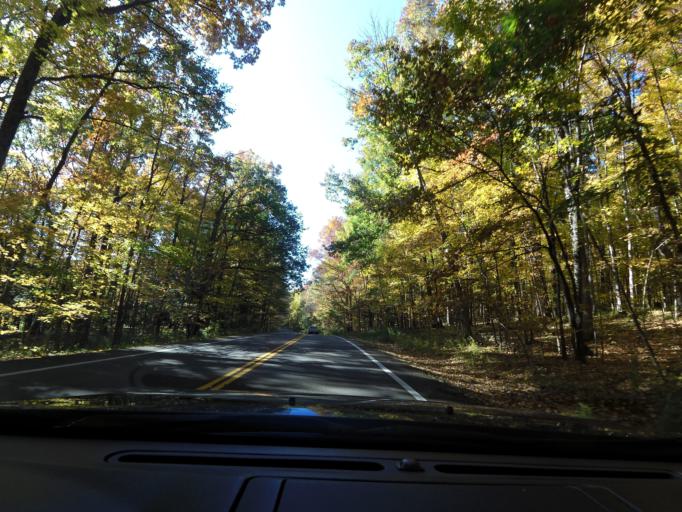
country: US
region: New York
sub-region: Wyoming County
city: Castile
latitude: 42.6453
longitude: -77.9848
